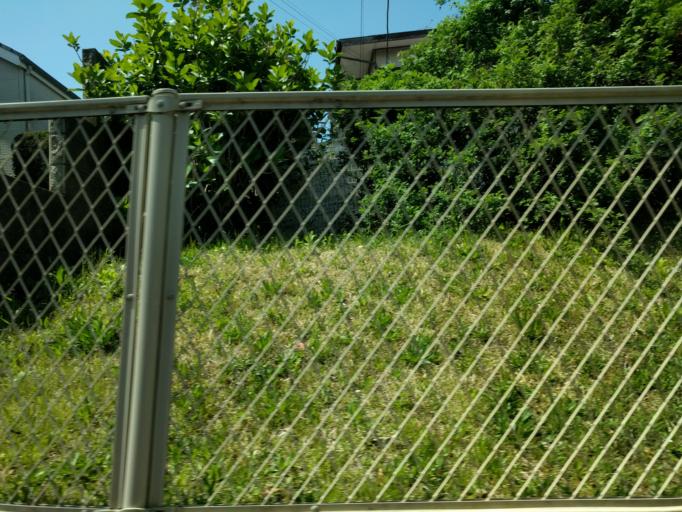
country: JP
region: Tokyo
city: Mitaka-shi
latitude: 35.6514
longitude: 139.5998
